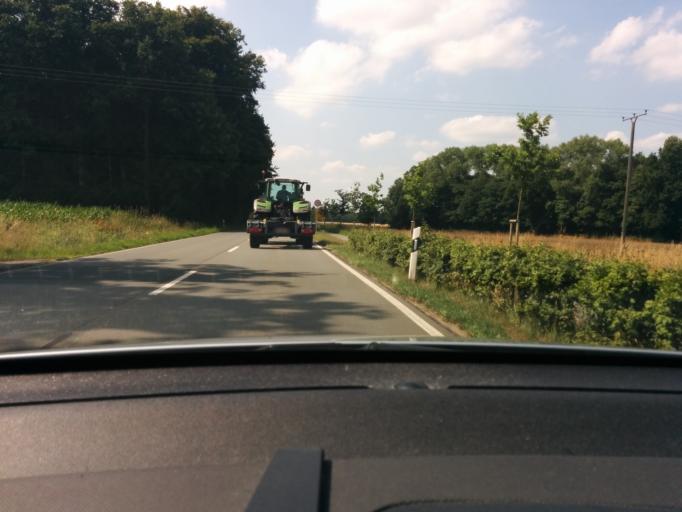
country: DE
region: North Rhine-Westphalia
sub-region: Regierungsbezirk Munster
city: Wettringen
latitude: 52.1775
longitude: 7.2795
